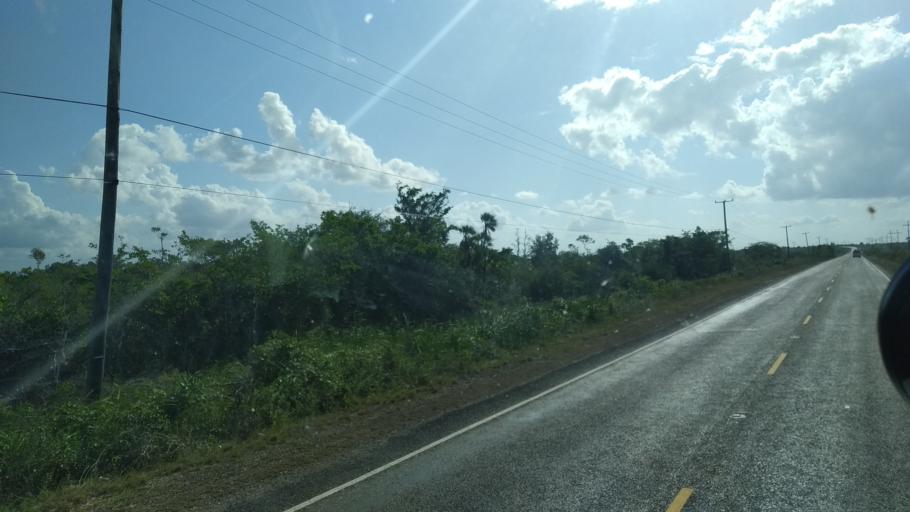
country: BZ
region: Belize
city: Belize City
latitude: 17.4057
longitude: -88.4893
